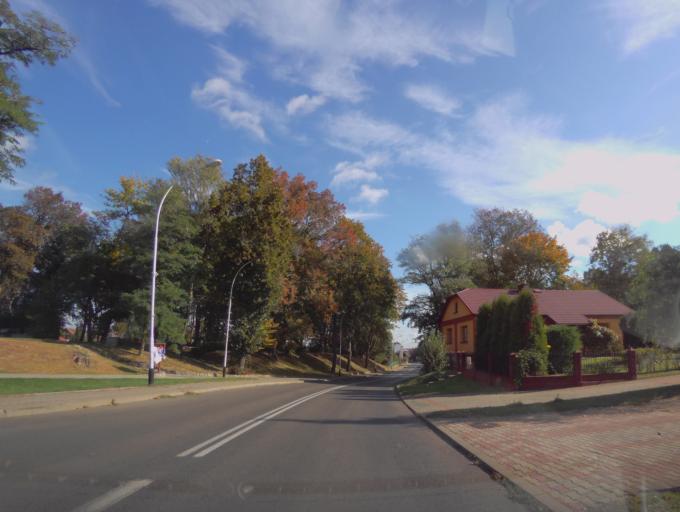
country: PL
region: Subcarpathian Voivodeship
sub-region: Powiat lezajski
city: Lezajsk
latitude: 50.2503
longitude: 22.4157
